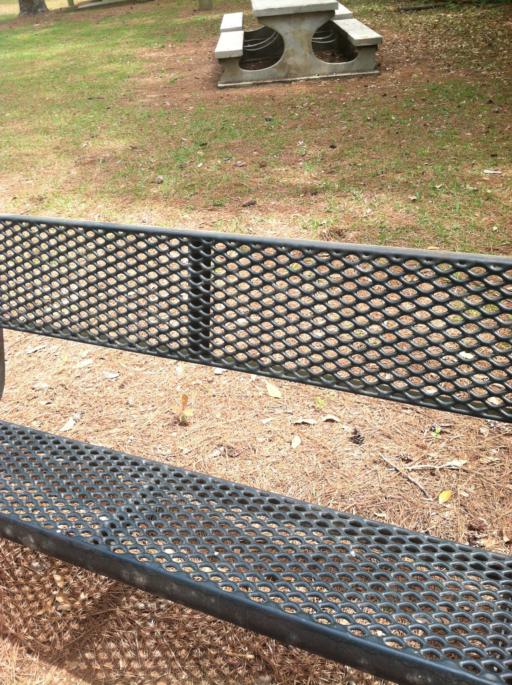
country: US
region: Georgia
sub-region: Early County
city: Blakely
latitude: 31.4682
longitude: -84.9272
